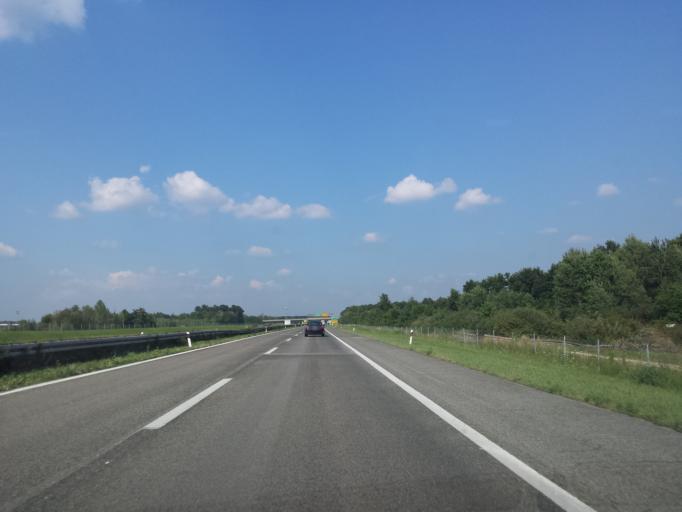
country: HR
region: Zagrebacka
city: Jastrebarsko
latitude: 45.6411
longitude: 15.6735
